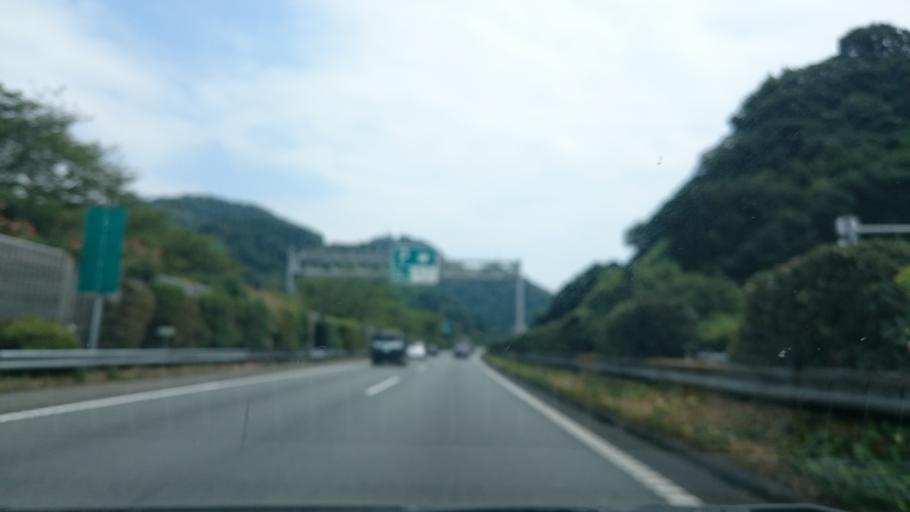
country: JP
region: Shizuoka
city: Shizuoka-shi
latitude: 35.0659
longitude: 138.5277
